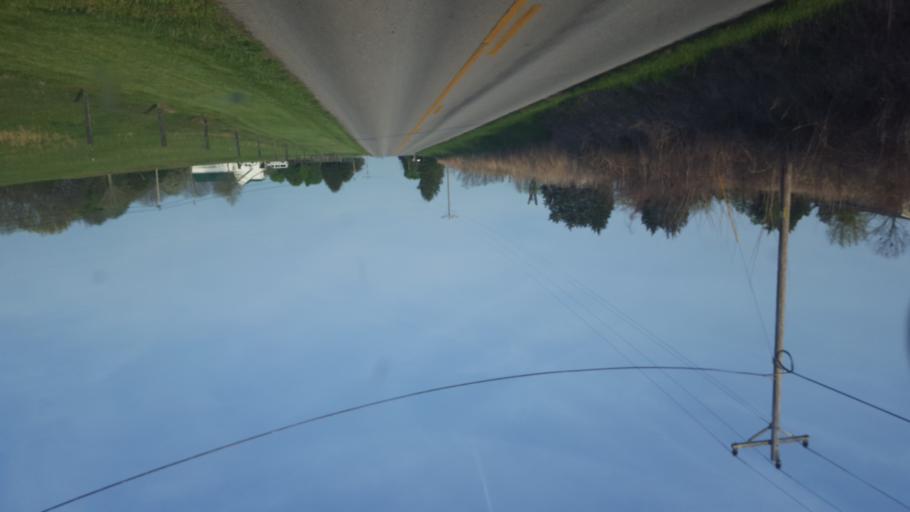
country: US
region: Kentucky
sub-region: Barren County
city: Glasgow
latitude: 36.9368
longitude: -86.0798
